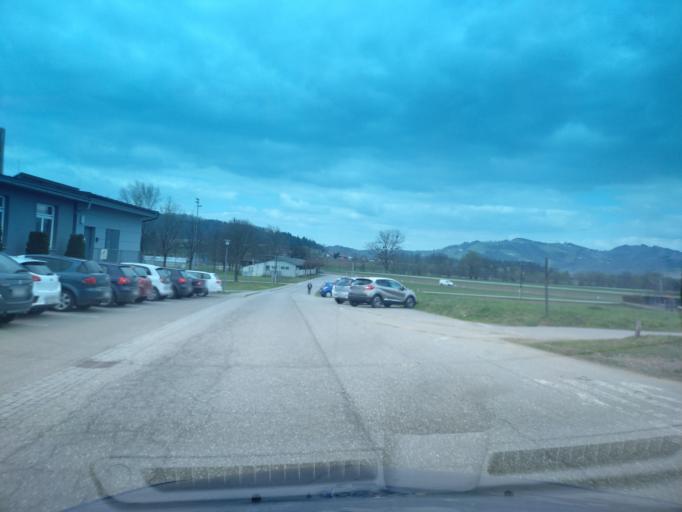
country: AT
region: Styria
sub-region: Politischer Bezirk Leibnitz
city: Grossklein
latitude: 46.7370
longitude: 15.4381
